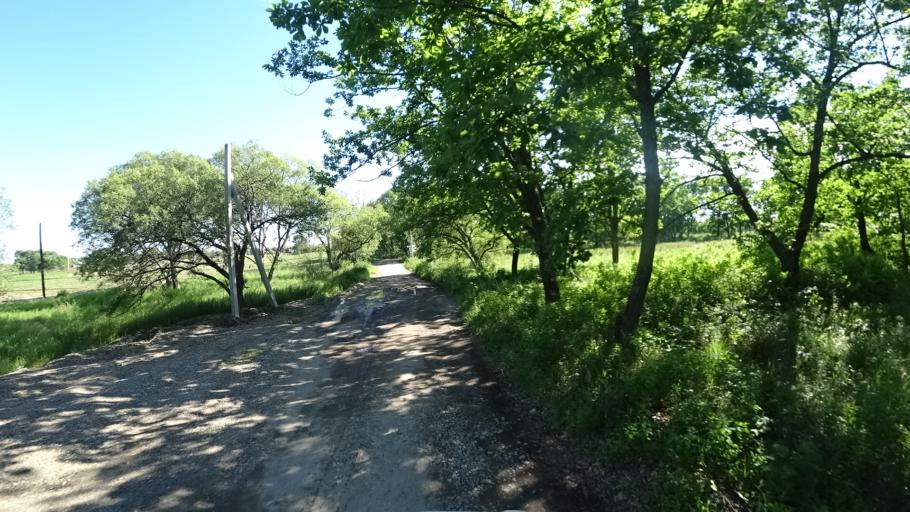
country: RU
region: Khabarovsk Krai
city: Khor
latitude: 47.8879
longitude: 135.0200
